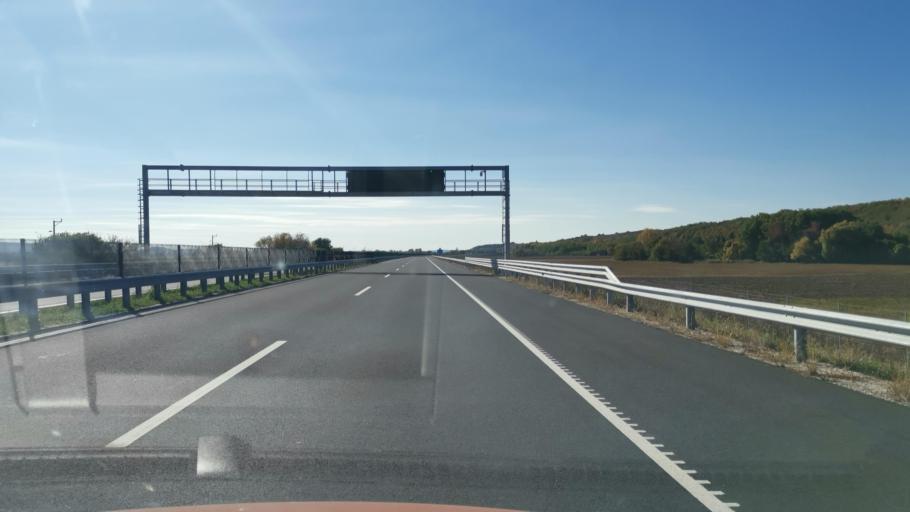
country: HU
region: Borsod-Abauj-Zemplen
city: Gonc
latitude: 48.4385
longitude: 21.1886
